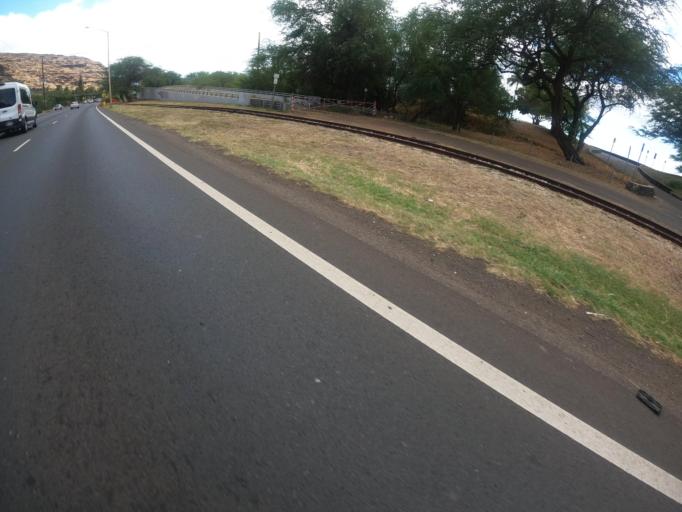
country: US
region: Hawaii
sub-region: Honolulu County
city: Nanakuli
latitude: 21.3768
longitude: -158.1406
